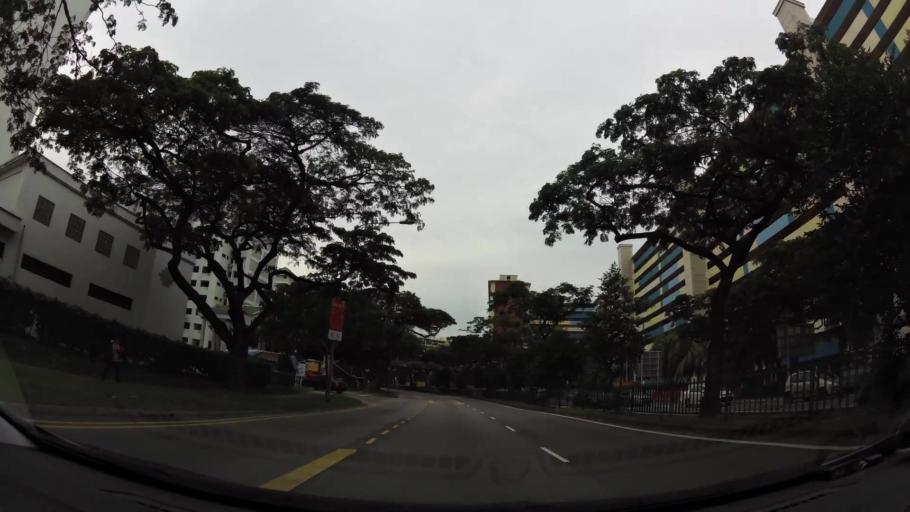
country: SG
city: Singapore
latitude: 1.3625
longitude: 103.8929
